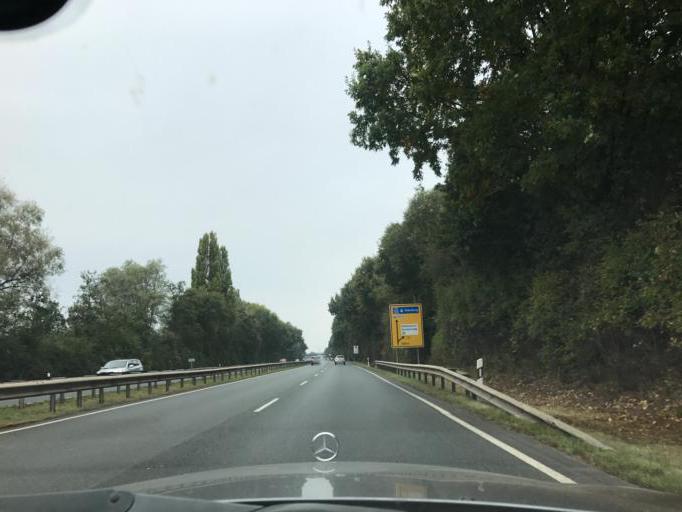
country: DE
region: Bremen
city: Bremen
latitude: 53.0442
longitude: 8.8333
